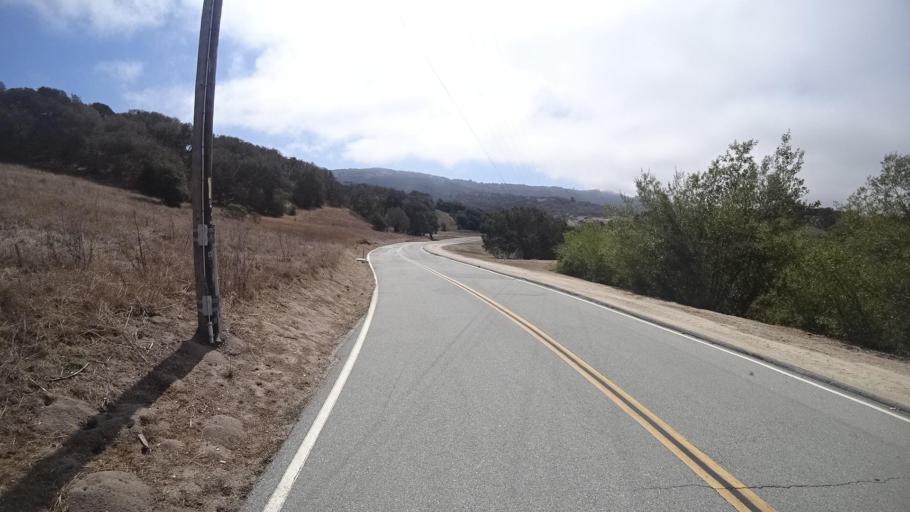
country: US
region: California
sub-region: Monterey County
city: Carmel Valley Village
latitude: 36.5747
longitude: -121.7644
